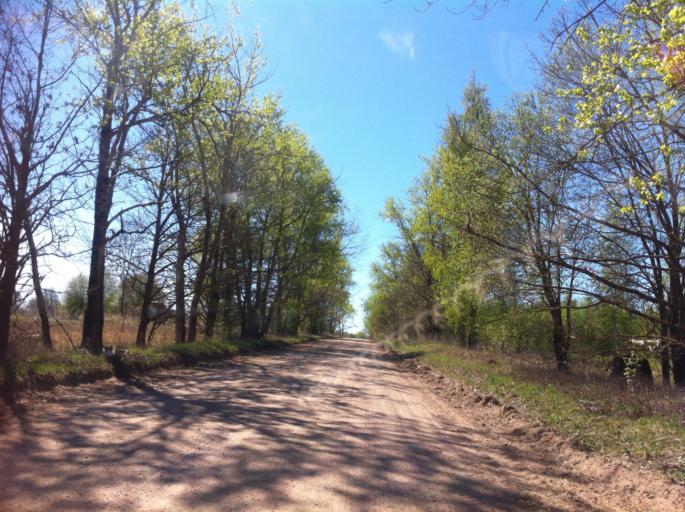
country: RU
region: Pskov
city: Izborsk
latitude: 57.7922
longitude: 27.9634
